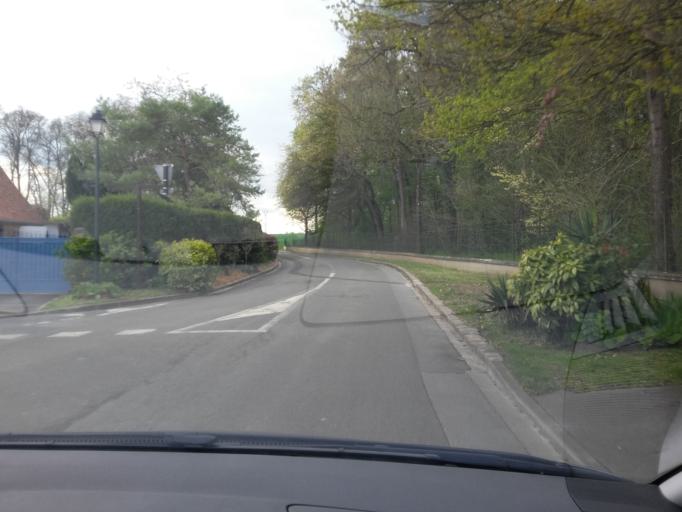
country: FR
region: Picardie
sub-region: Departement de l'Oise
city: Longueil-Sainte-Marie
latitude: 49.3700
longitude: 2.7011
